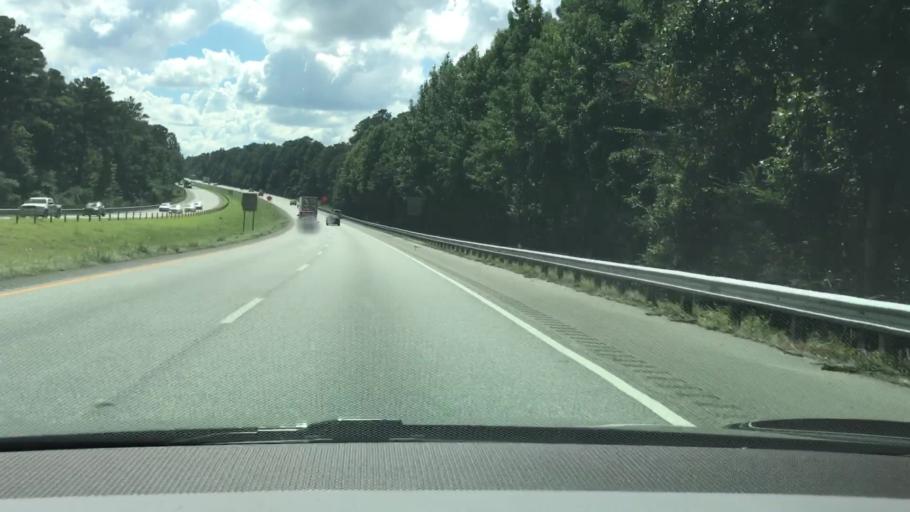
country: US
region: Alabama
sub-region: Lee County
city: Auburn
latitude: 32.5961
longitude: -85.4490
